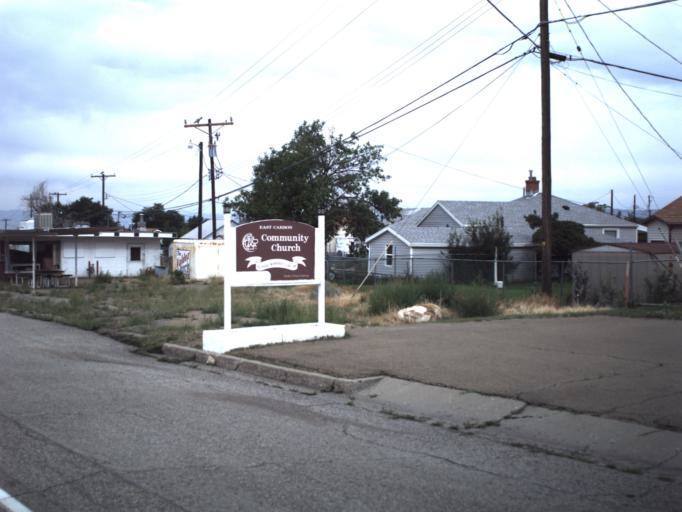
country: US
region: Utah
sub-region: Carbon County
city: East Carbon City
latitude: 39.5421
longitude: -110.4213
